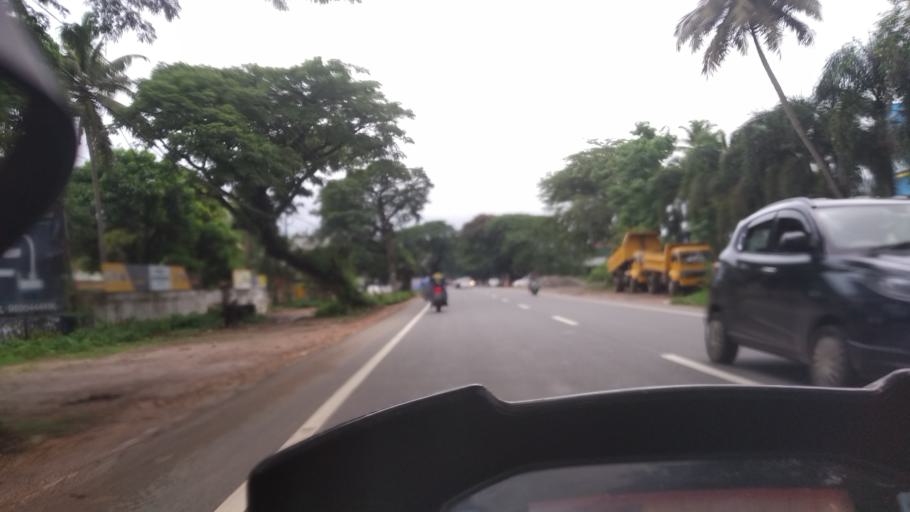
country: IN
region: Kerala
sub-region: Alappuzha
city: Alleppey
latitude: 9.4580
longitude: 76.3404
